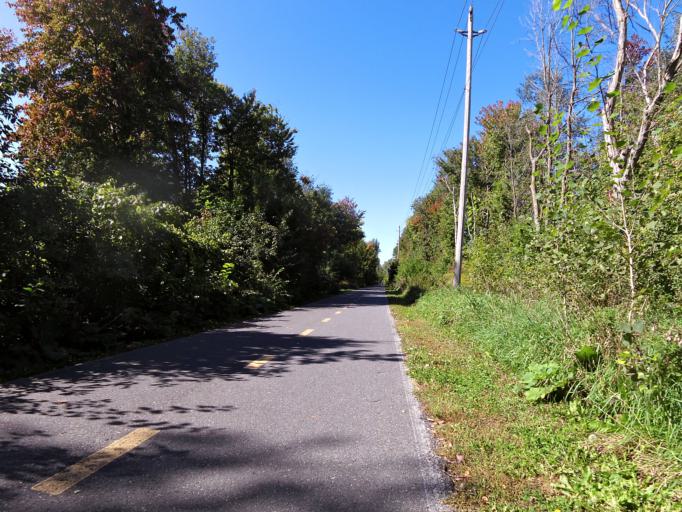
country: CA
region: Ontario
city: Bourget
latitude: 45.2720
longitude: -75.2993
